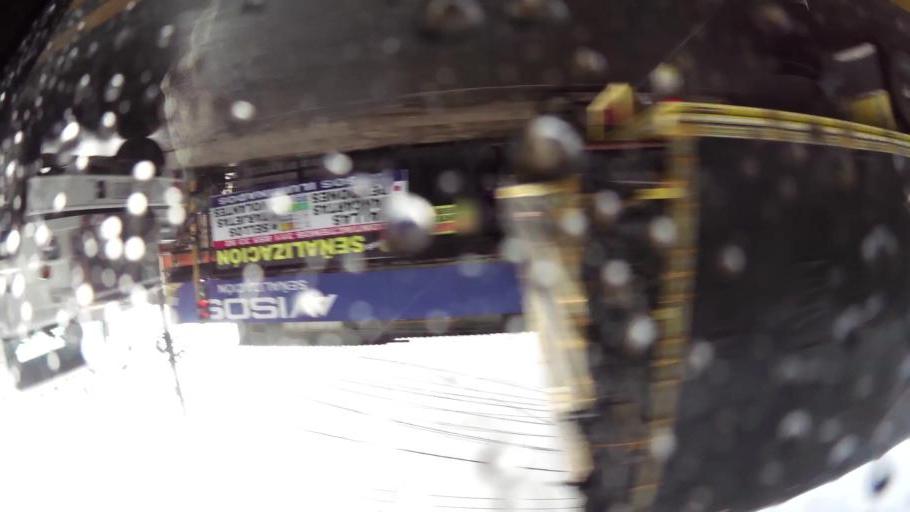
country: CO
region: Cundinamarca
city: Chia
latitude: 4.8523
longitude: -74.0628
